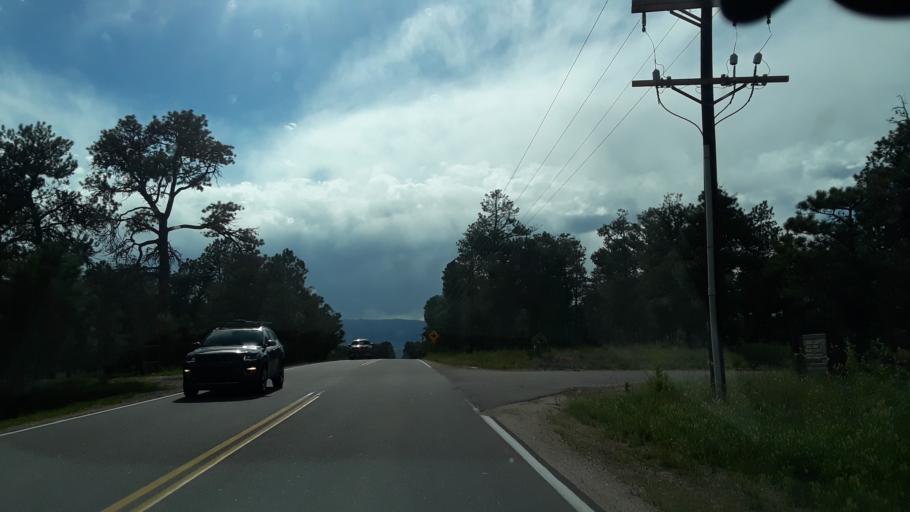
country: US
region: Colorado
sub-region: El Paso County
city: Black Forest
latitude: 39.0128
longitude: -104.7346
